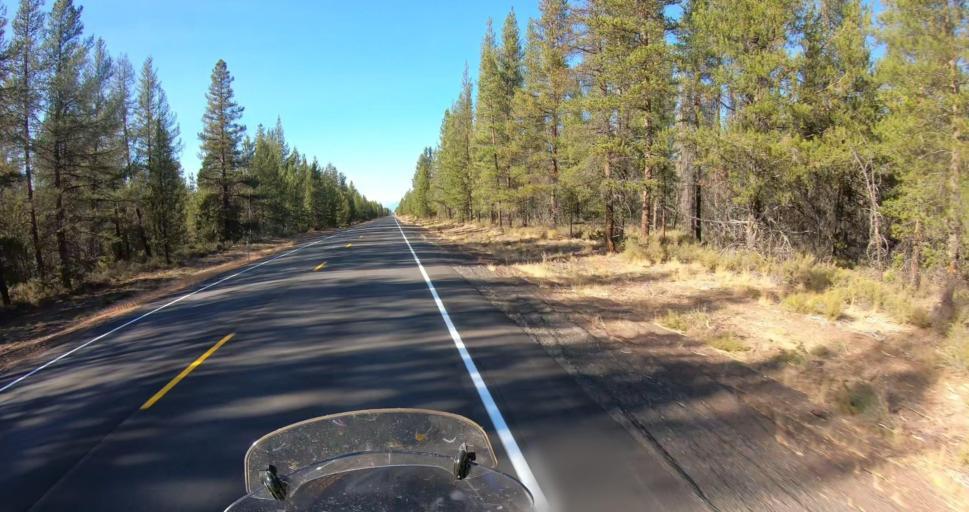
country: US
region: Oregon
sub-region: Deschutes County
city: La Pine
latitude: 43.5280
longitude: -121.4596
